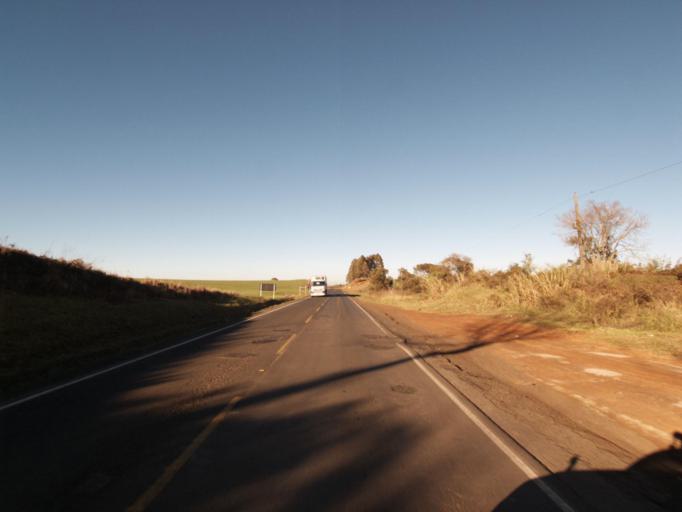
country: AR
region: Misiones
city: Bernardo de Irigoyen
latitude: -26.3169
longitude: -53.5493
